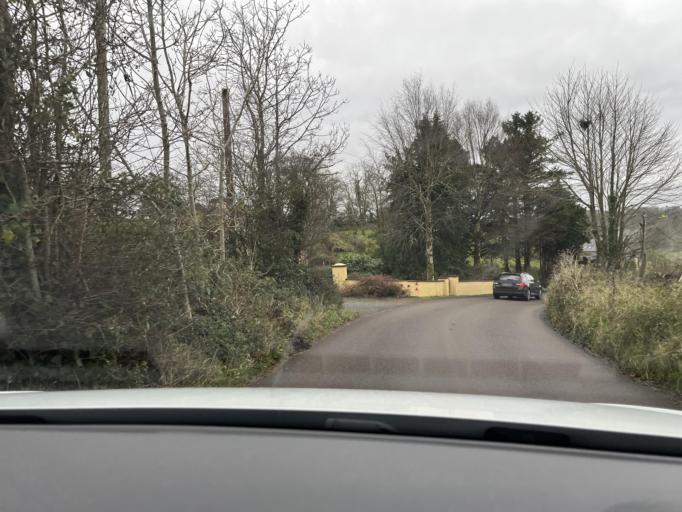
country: IE
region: Connaught
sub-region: County Leitrim
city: Manorhamilton
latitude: 54.2329
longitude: -8.2826
